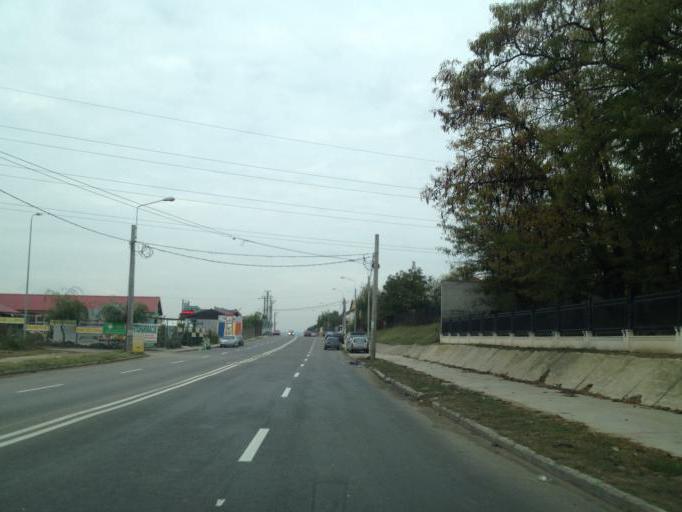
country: RO
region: Dolj
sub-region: Municipiul Craiova
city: Facai
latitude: 44.2929
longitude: 23.8121
